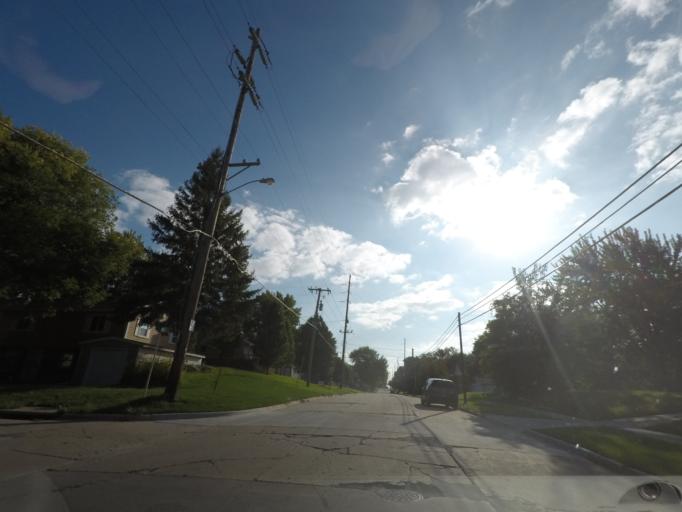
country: US
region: Iowa
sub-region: Story County
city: Nevada
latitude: 42.0156
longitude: -93.4551
